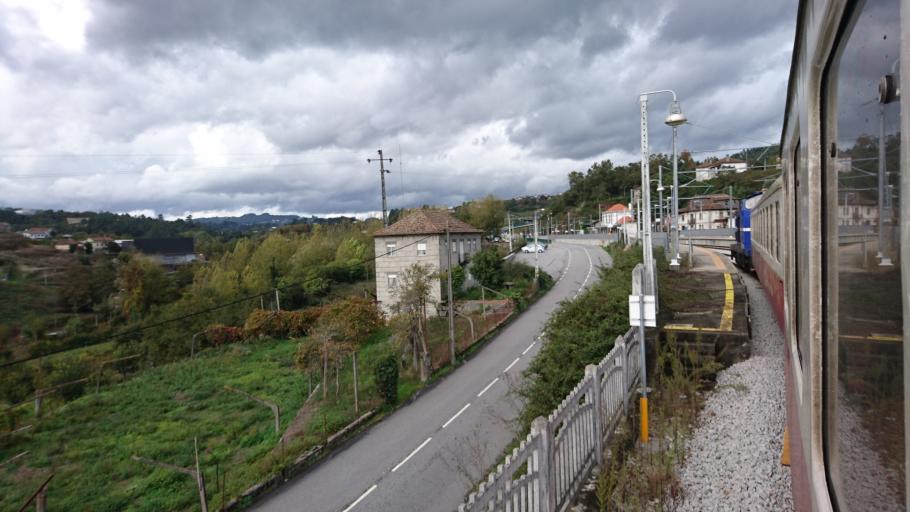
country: PT
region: Porto
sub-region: Marco de Canaveses
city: Marco de Canavezes
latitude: 41.2154
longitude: -8.1544
